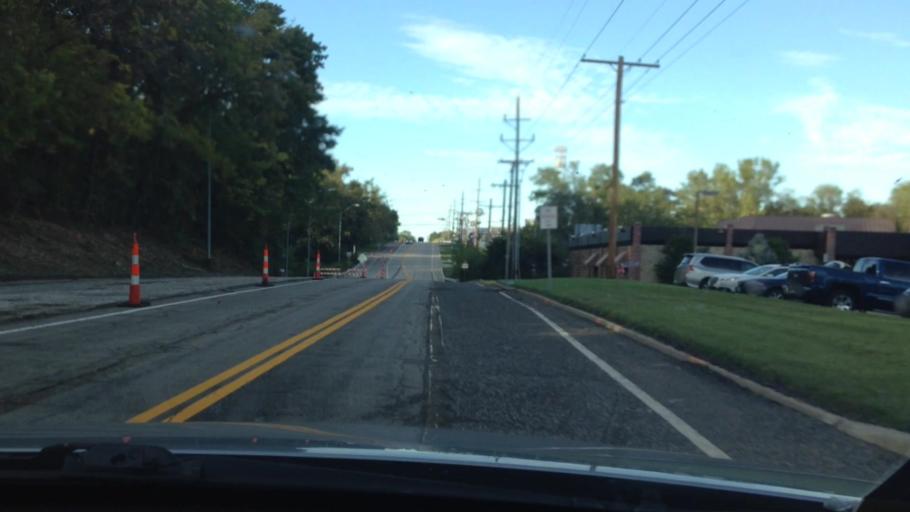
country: US
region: Missouri
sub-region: Clay County
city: North Kansas City
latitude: 39.1621
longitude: -94.5769
